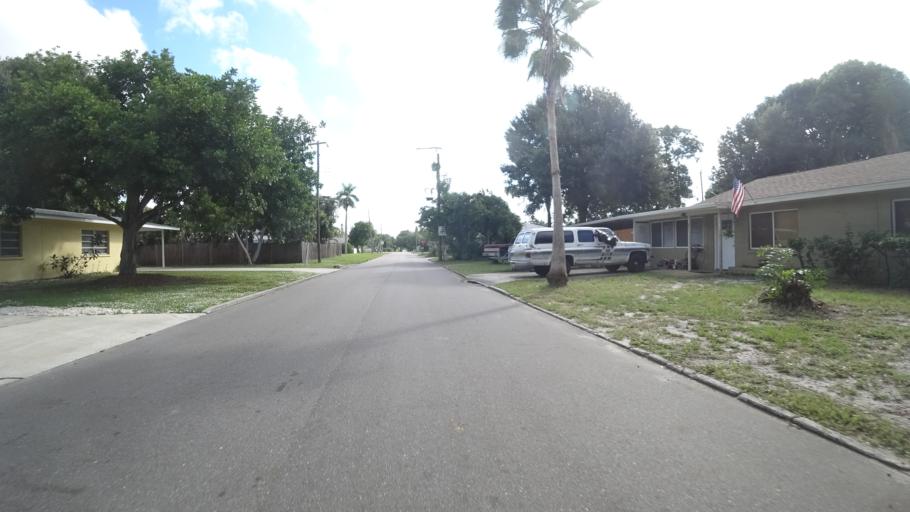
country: US
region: Florida
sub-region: Manatee County
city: West Bradenton
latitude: 27.4977
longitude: -82.6119
